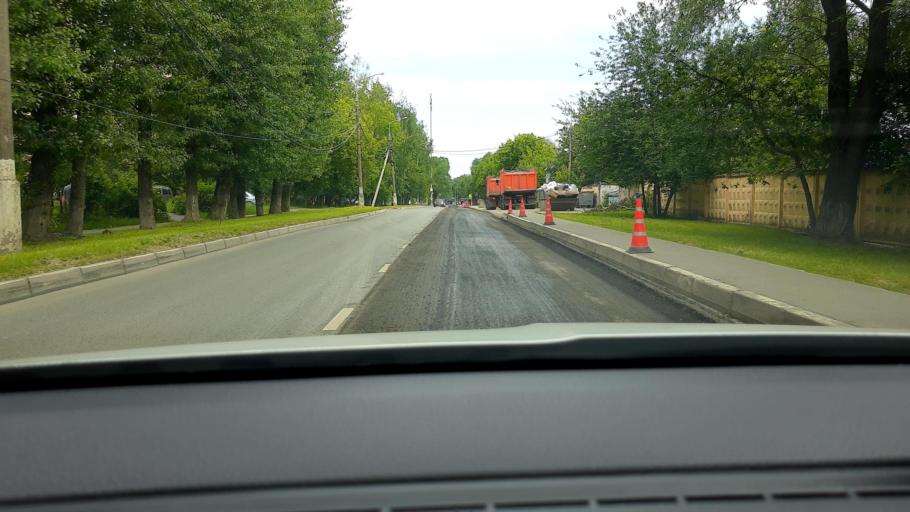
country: RU
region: Moskovskaya
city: Shcherbinka
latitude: 55.4739
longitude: 37.5448
